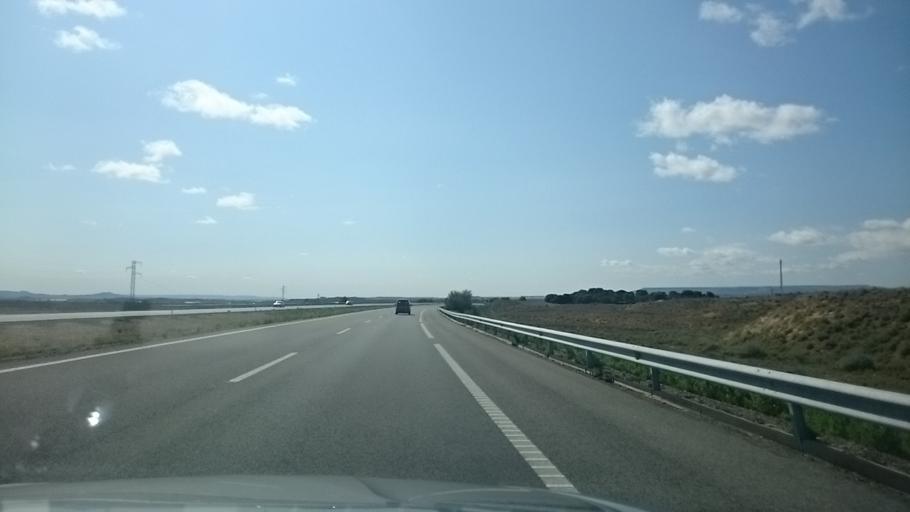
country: ES
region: Navarre
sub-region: Provincia de Navarra
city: Murchante
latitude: 42.0749
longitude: -1.6968
